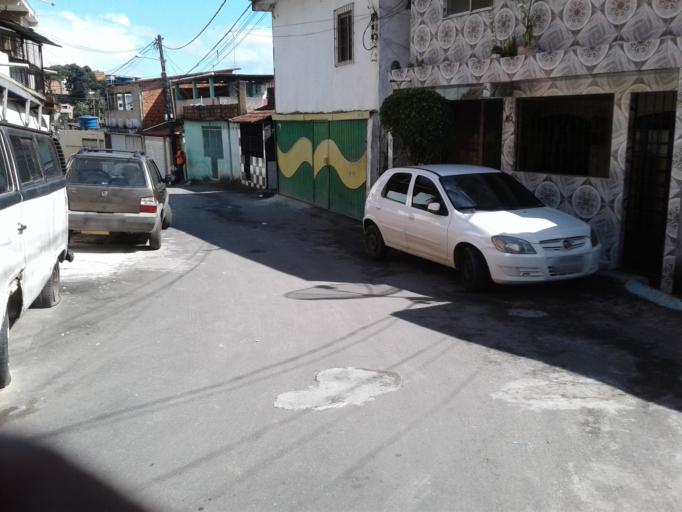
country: BR
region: Bahia
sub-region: Salvador
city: Salvador
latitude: -12.9112
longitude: -38.4706
